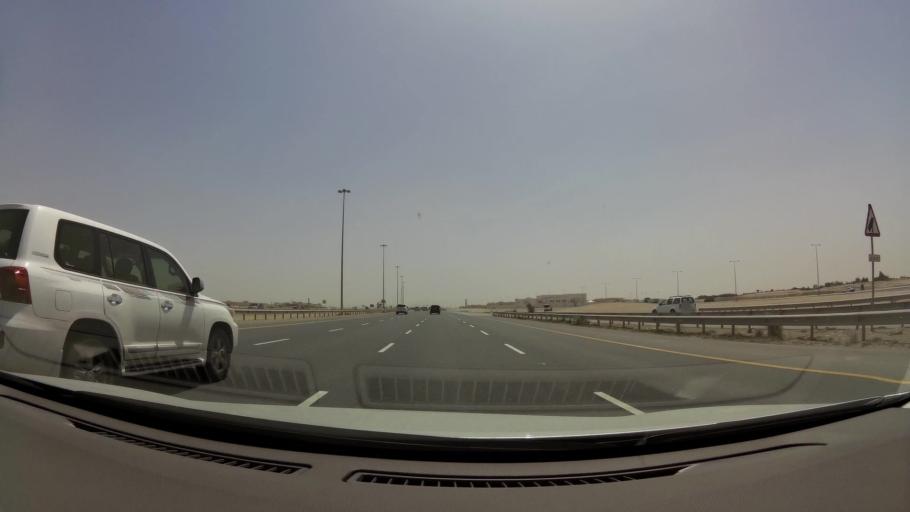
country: QA
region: Baladiyat Umm Salal
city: Umm Salal Muhammad
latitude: 25.4428
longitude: 51.4104
